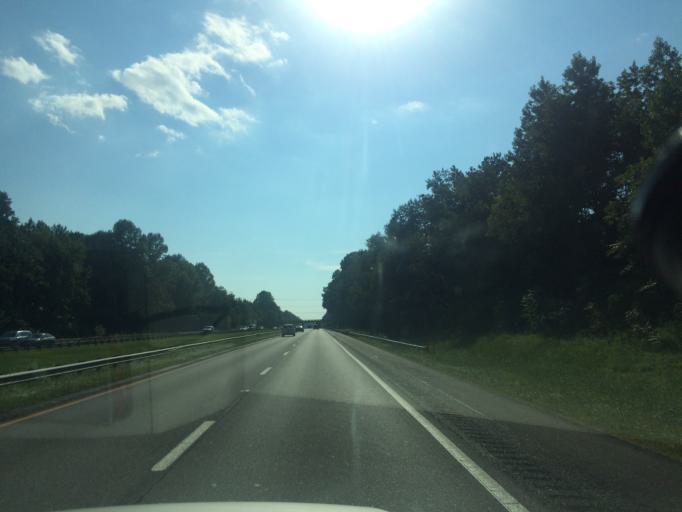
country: US
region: North Carolina
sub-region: Cleveland County
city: White Plains
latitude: 35.1711
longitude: -81.4299
